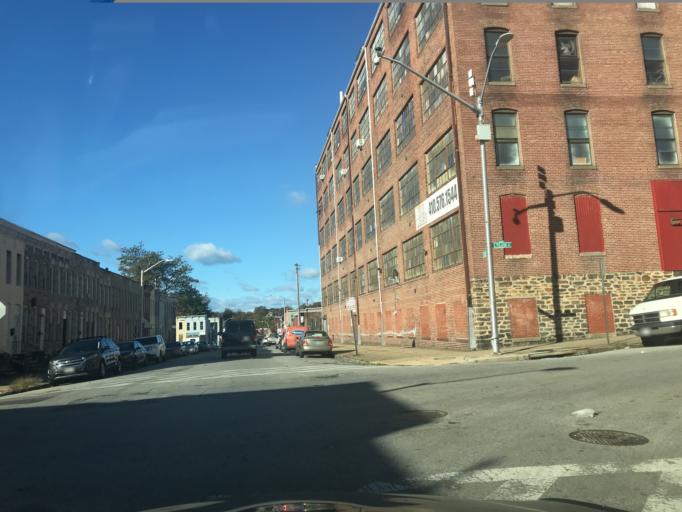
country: US
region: Maryland
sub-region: City of Baltimore
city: Baltimore
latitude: 39.2841
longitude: -76.6497
